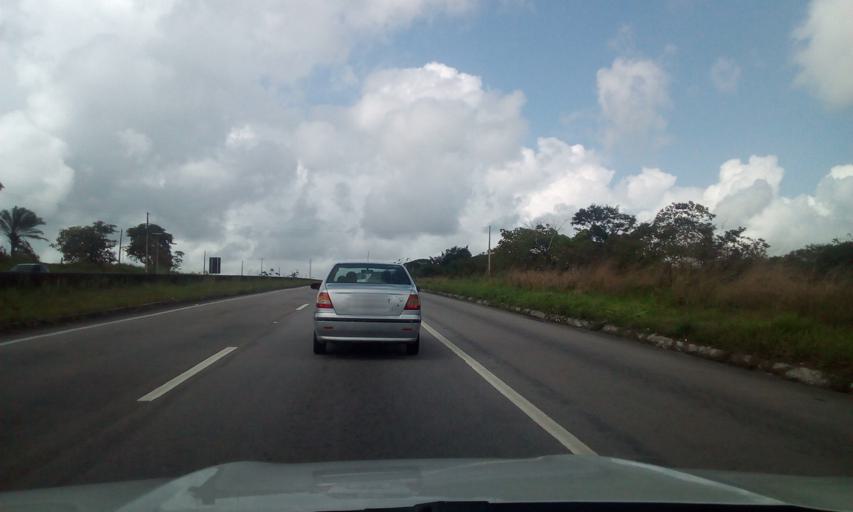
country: BR
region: Paraiba
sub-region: Alhandra
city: Alhandra
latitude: -7.4411
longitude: -34.9779
